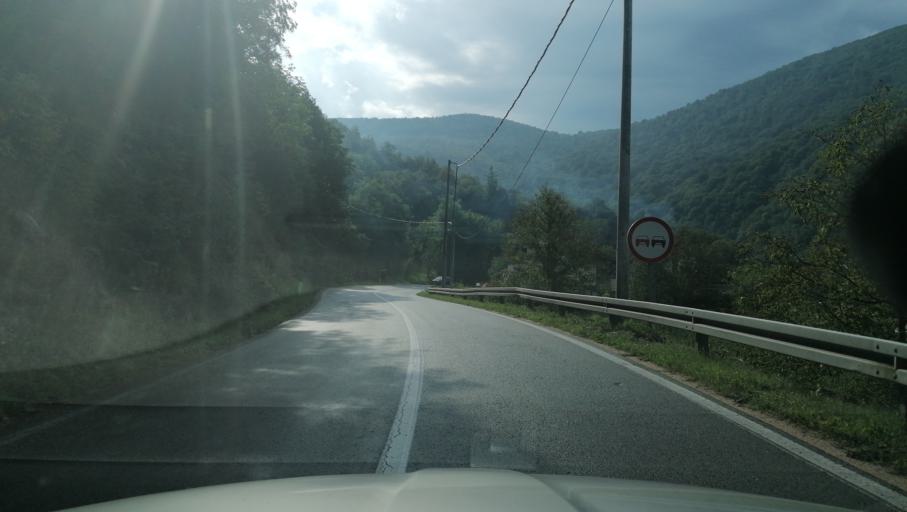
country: BA
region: Republika Srpska
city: Hiseti
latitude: 44.6744
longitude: 17.1532
